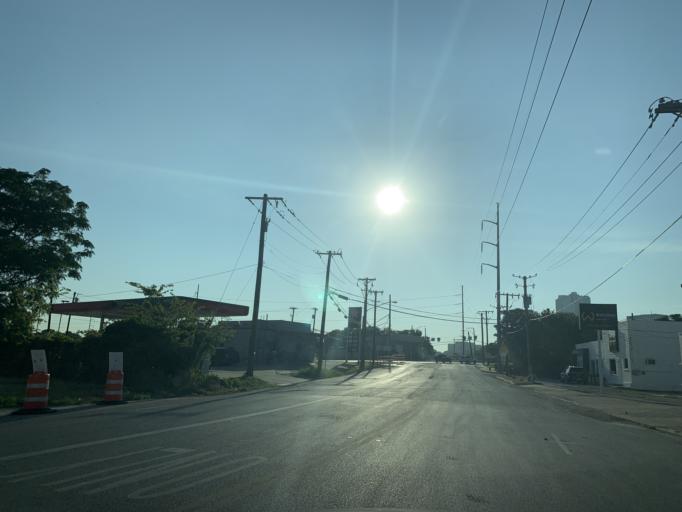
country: US
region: Texas
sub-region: Tarrant County
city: Fort Worth
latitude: 32.7589
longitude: -97.3448
